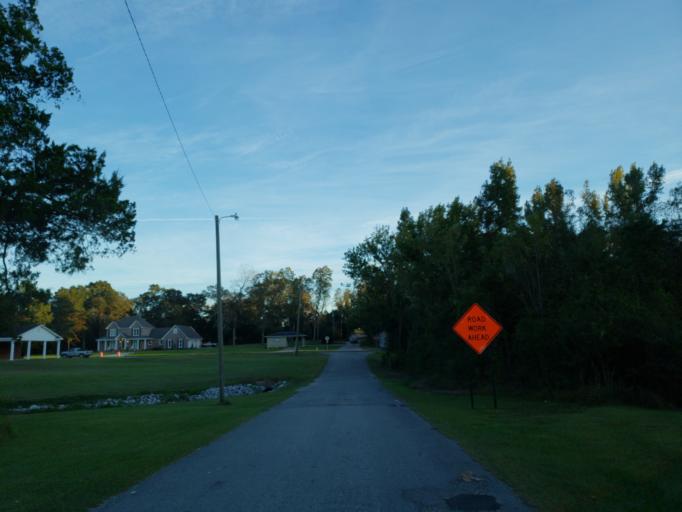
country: US
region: Mississippi
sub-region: Wayne County
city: Belmont
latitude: 31.4352
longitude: -88.4760
